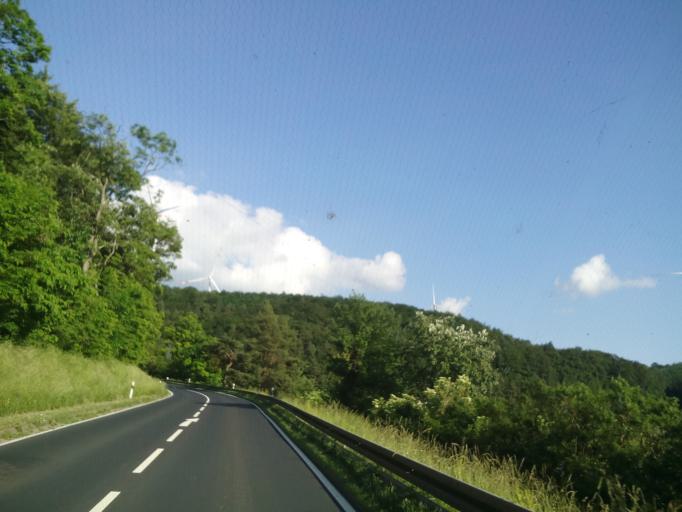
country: DE
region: Bavaria
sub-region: Regierungsbezirk Unterfranken
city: Nudlingen
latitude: 50.2249
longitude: 10.1454
